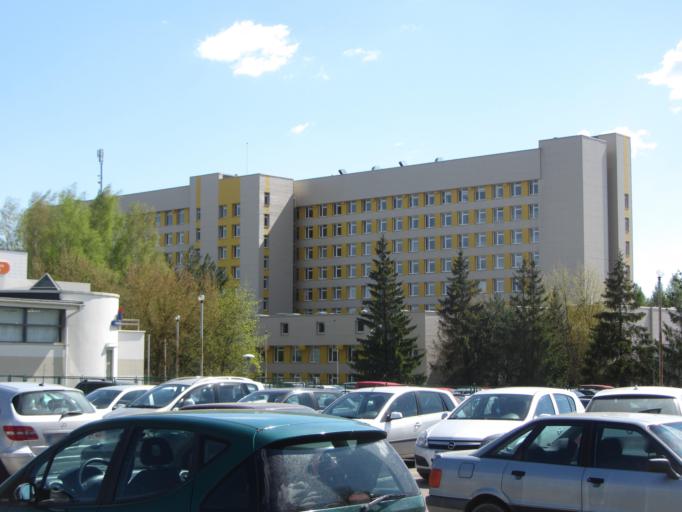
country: LT
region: Vilnius County
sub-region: Vilnius
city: Fabijoniskes
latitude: 54.7532
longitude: 25.2807
